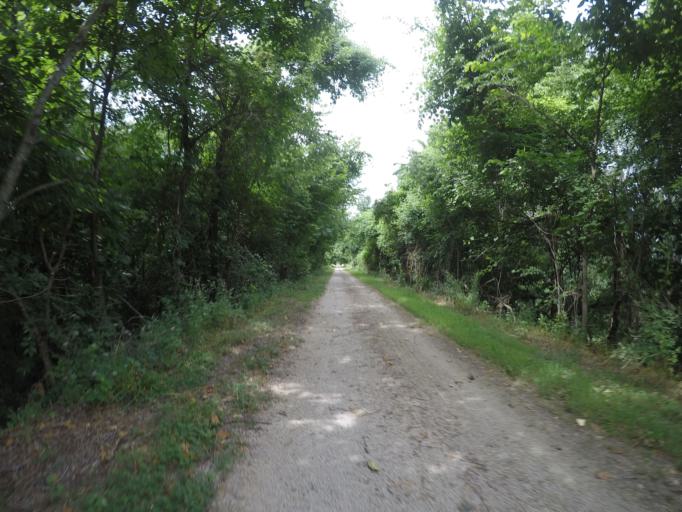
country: US
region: Kansas
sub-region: Anderson County
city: Garnett
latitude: 38.3369
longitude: -95.2421
